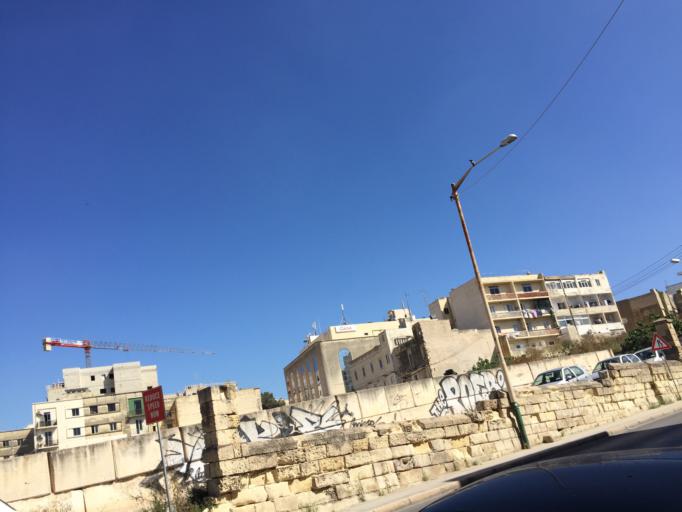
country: MT
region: Ta' Xbiex
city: Ta' Xbiex
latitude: 35.9010
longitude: 14.4911
